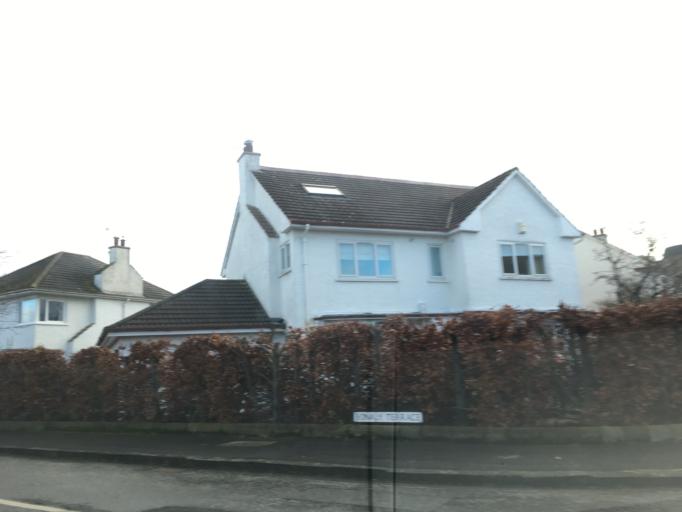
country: GB
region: Scotland
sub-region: Edinburgh
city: Colinton
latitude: 55.9020
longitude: -3.2582
